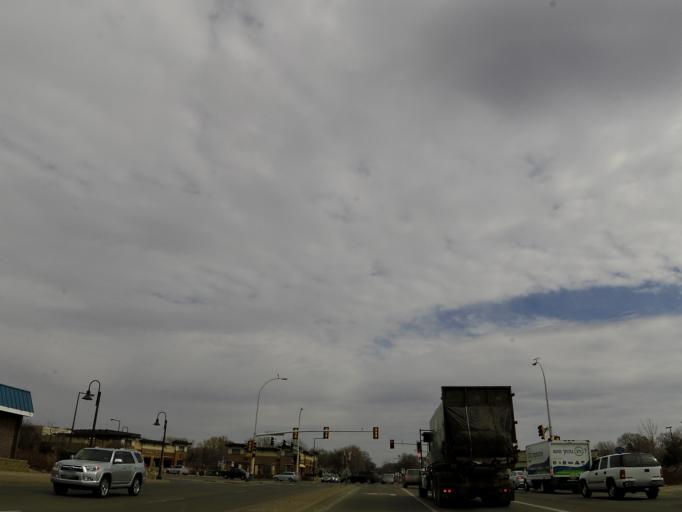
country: US
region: Minnesota
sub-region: Scott County
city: Savage
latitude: 44.8102
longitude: -93.3305
